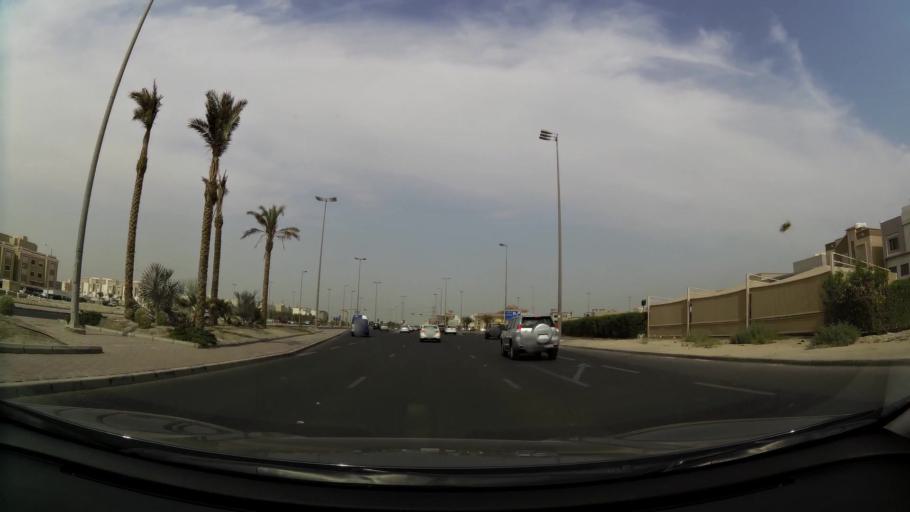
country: KW
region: Al Farwaniyah
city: Janub as Surrah
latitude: 29.2960
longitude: 48.0028
